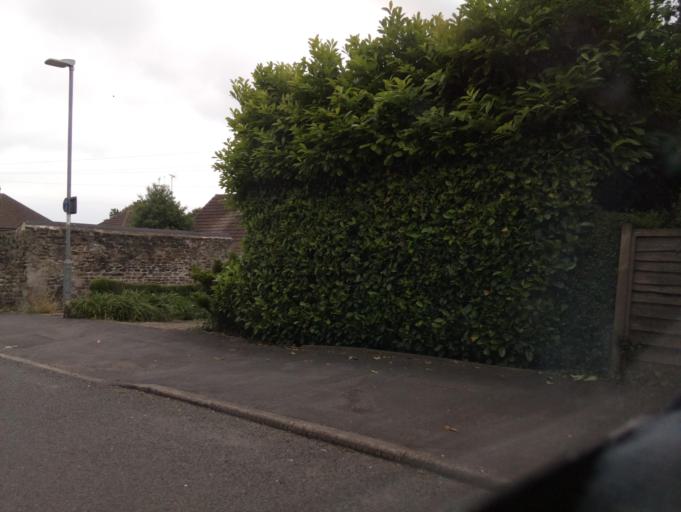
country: GB
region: England
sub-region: District of Rutland
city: Oakham
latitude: 52.6709
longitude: -0.7427
